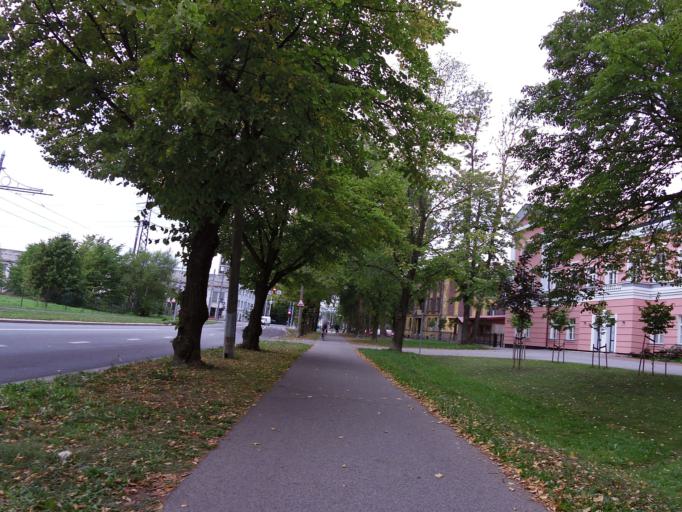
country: EE
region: Harju
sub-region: Tallinna linn
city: Tallinn
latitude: 59.4478
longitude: 24.7135
